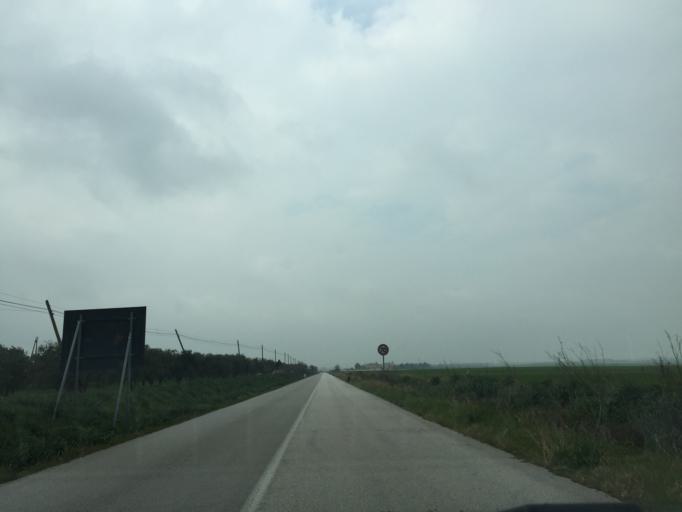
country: IT
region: Apulia
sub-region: Provincia di Foggia
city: Castelluccio dei Sauri
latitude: 41.3994
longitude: 15.4270
